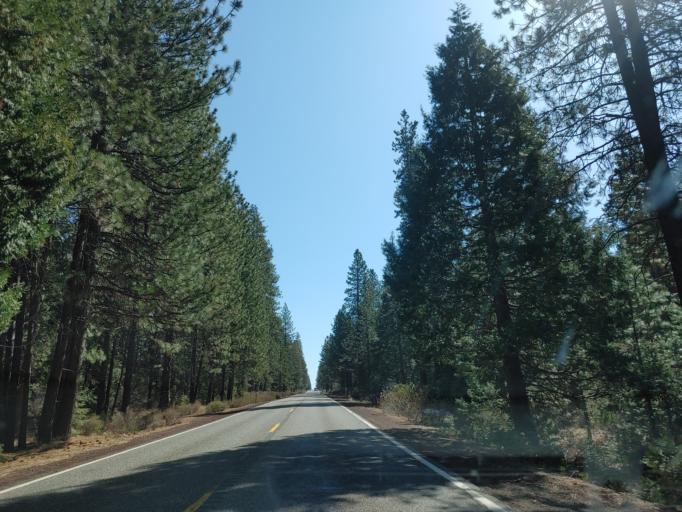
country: US
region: California
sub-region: Siskiyou County
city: McCloud
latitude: 41.2547
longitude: -122.0661
